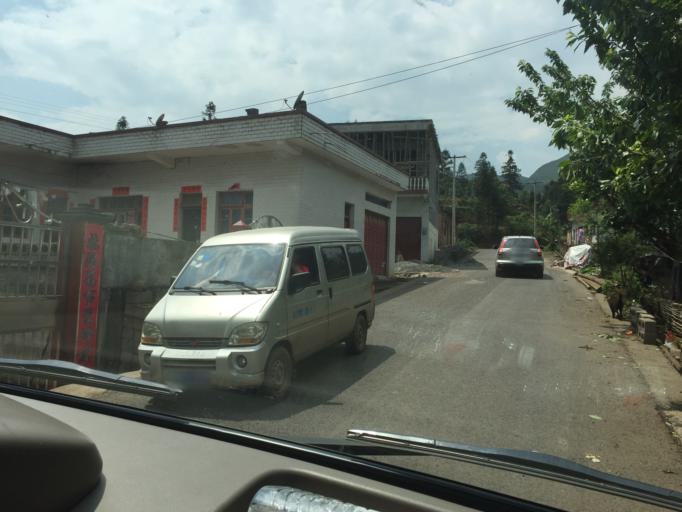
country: CN
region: Guangxi Zhuangzu Zizhiqu
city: Xinzhou
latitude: 25.6954
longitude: 105.2289
